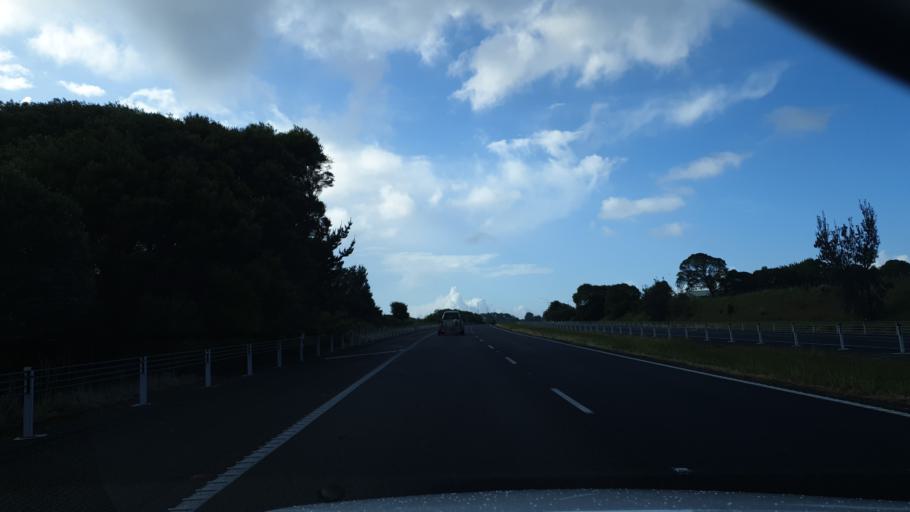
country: NZ
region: Auckland
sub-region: Auckland
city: Pukekohe East
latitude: -37.2457
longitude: 175.0268
